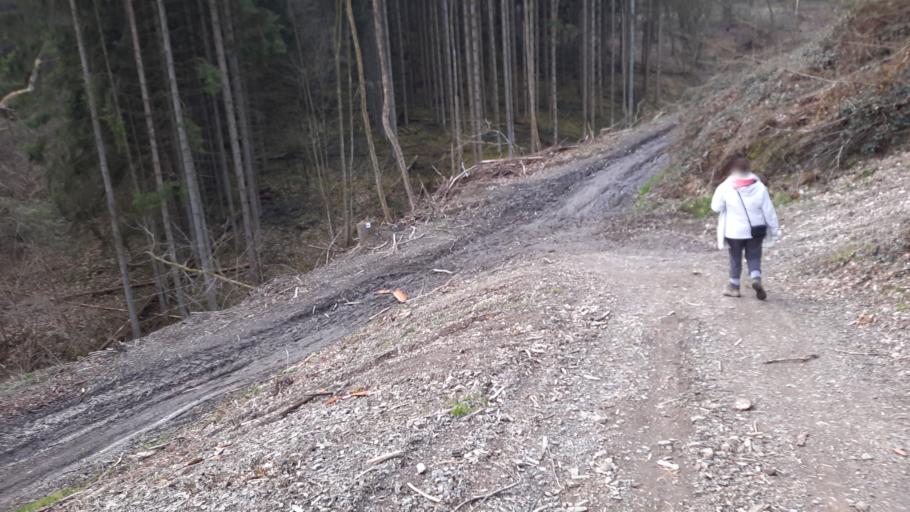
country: BE
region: Wallonia
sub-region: Province du Luxembourg
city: Rendeux
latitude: 50.2049
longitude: 5.5128
